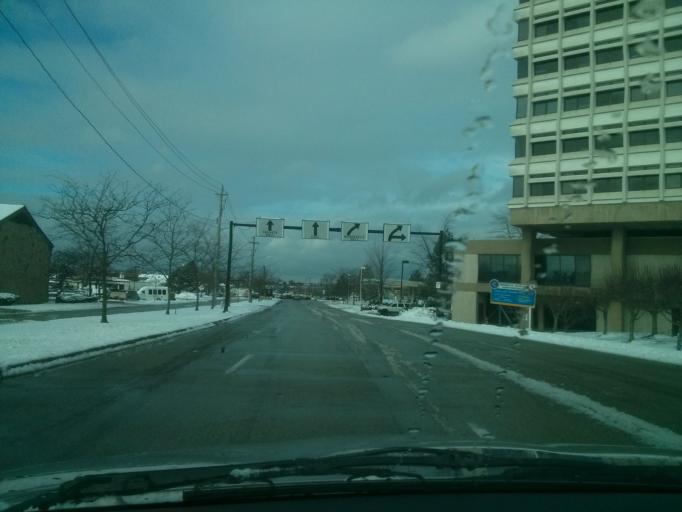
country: US
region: Ohio
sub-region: Cuyahoga County
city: Shaker Heights
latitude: 41.4631
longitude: -81.5342
